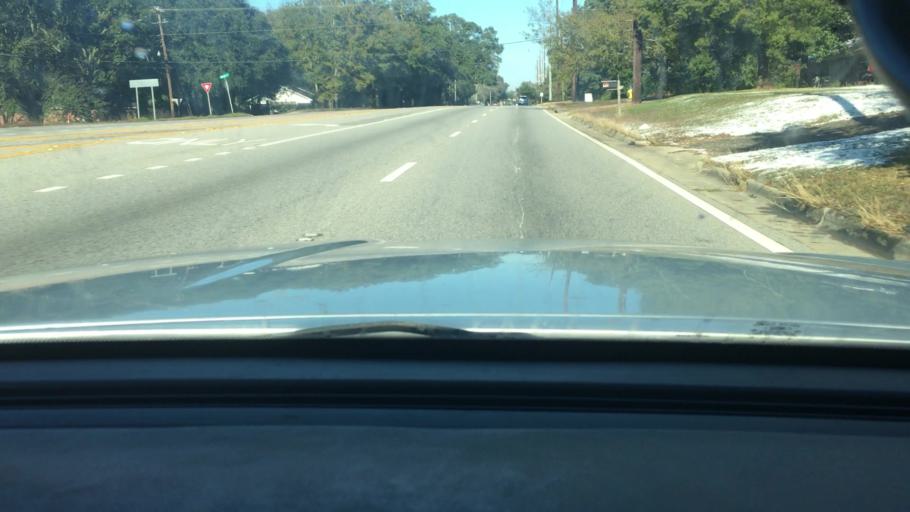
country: US
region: Alabama
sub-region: Mobile County
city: Prichard
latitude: 30.7225
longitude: -88.1655
